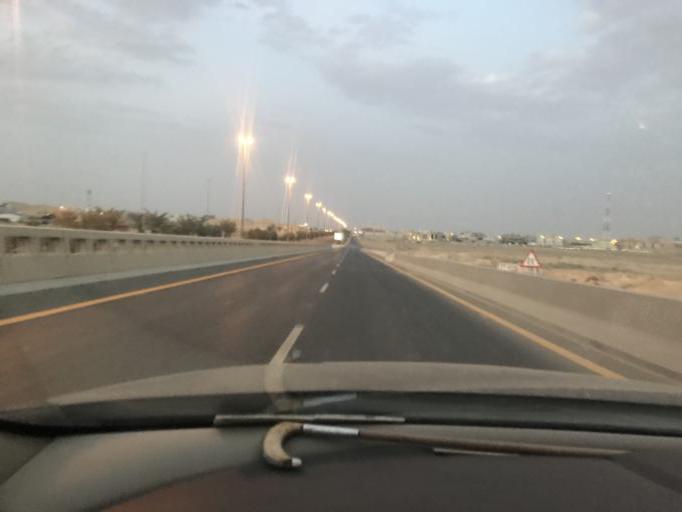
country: SA
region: Ar Riyad
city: Riyadh
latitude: 24.8443
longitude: 46.6572
